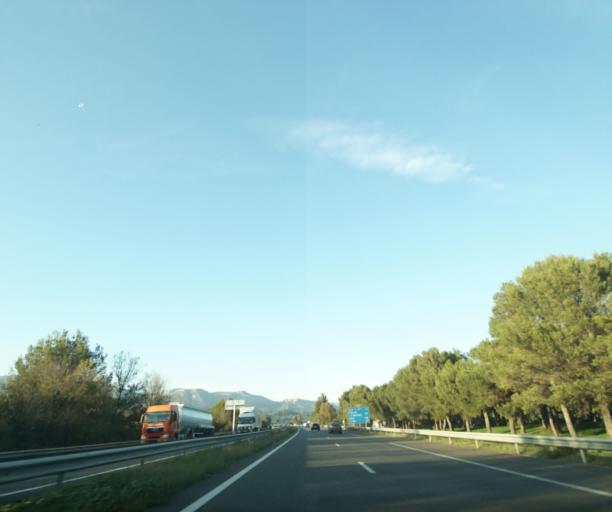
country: FR
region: Provence-Alpes-Cote d'Azur
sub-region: Departement des Bouches-du-Rhone
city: Aubagne
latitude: 43.3097
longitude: 5.5920
